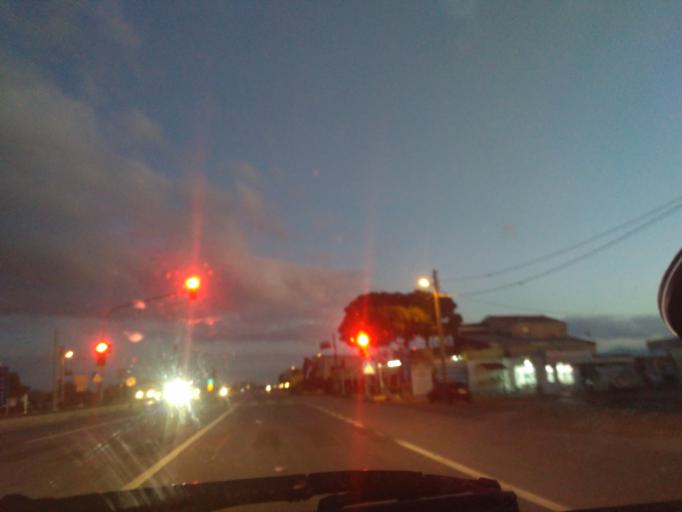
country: TR
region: Balikesir
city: Altinova
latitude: 39.1660
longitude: 26.8406
